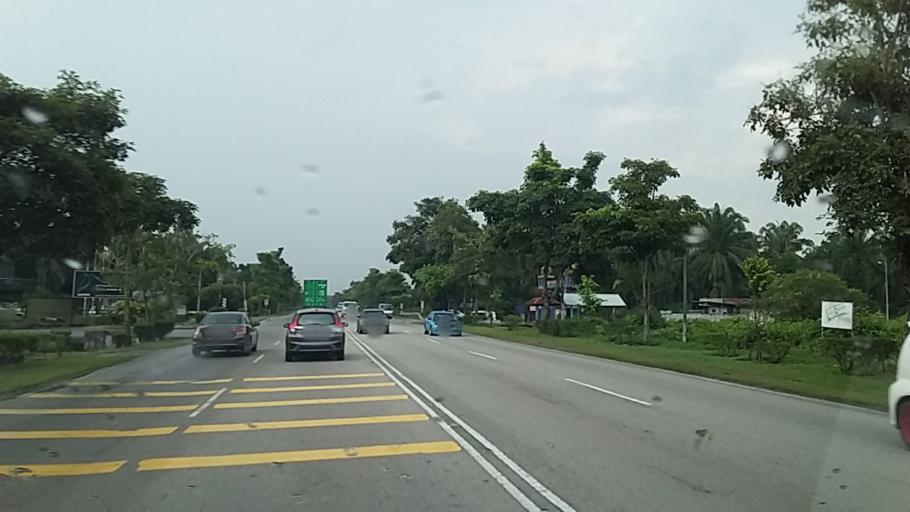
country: MY
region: Johor
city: Parit Raja
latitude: 1.8777
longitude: 103.1441
